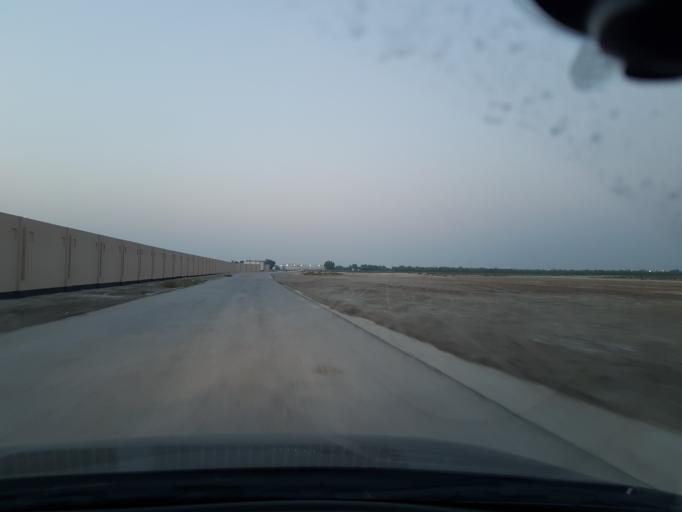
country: BH
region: Central Governorate
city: Dar Kulayb
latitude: 26.0074
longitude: 50.4750
